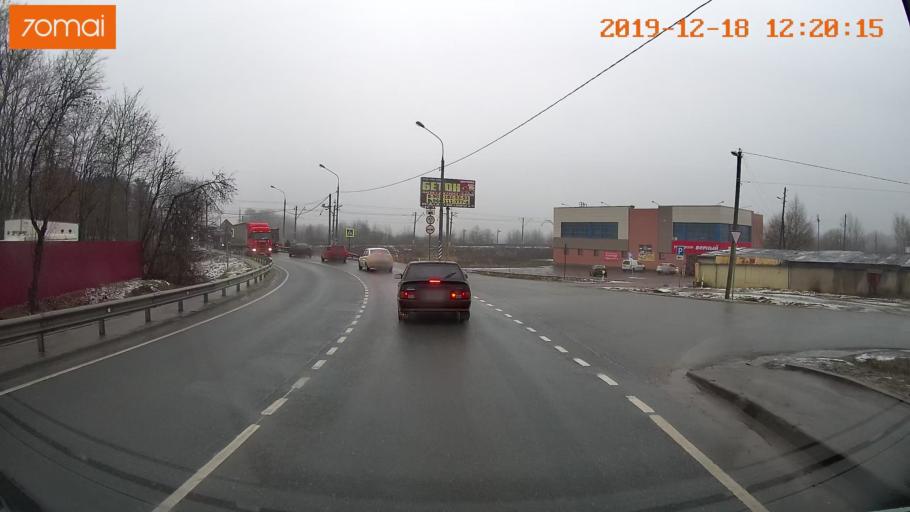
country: RU
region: Moskovskaya
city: Novopetrovskoye
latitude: 55.9960
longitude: 36.4740
